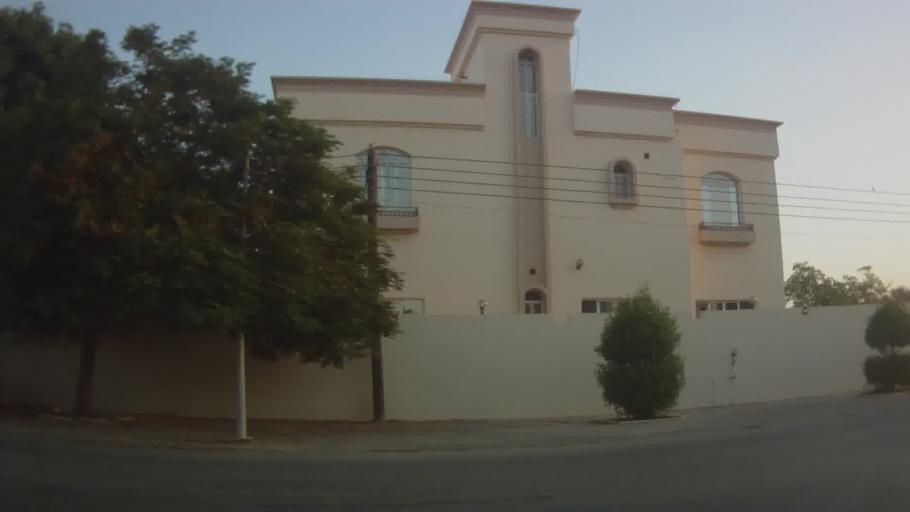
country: OM
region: Muhafazat Masqat
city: Bawshar
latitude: 23.5999
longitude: 58.4036
